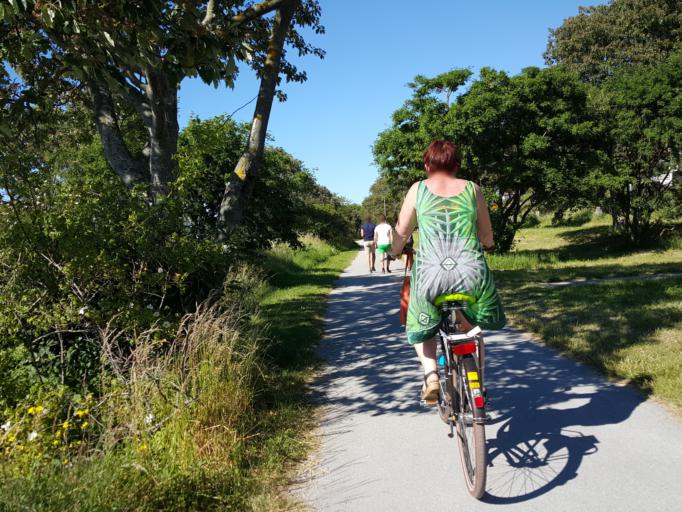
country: SE
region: Gotland
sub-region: Gotland
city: Visby
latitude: 57.6509
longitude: 18.3014
